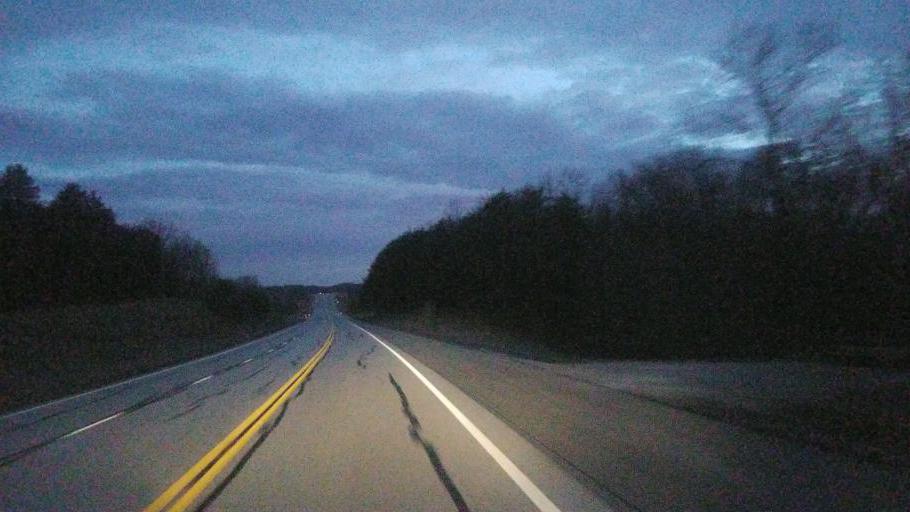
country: US
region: Tennessee
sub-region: Sequatchie County
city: Dunlap
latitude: 35.5198
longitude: -85.4701
